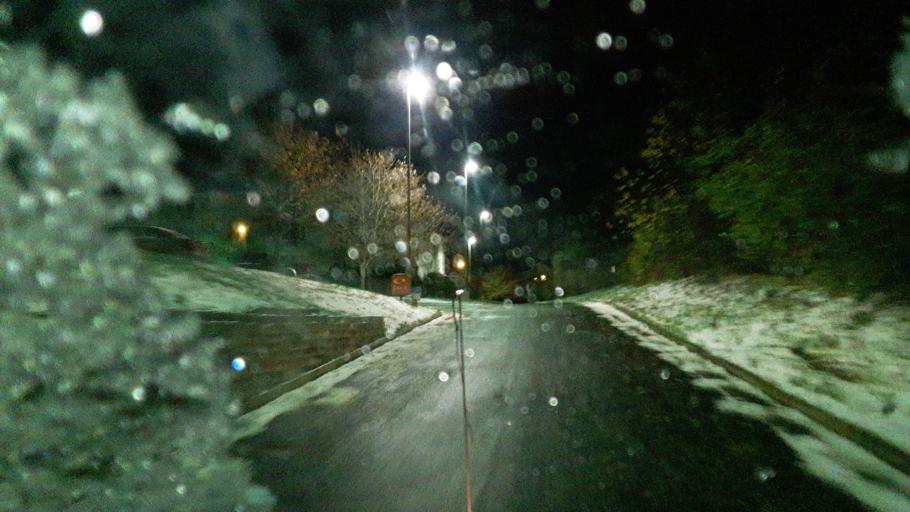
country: US
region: Ohio
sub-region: Portage County
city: Streetsboro
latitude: 41.2503
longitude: -81.3670
